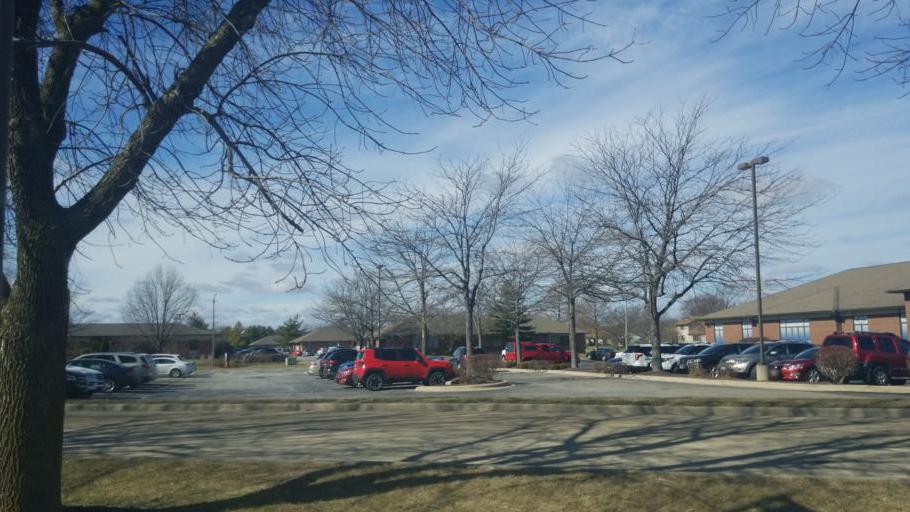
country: US
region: Illinois
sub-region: Sangamon County
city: Leland Grove
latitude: 39.7764
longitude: -89.7078
